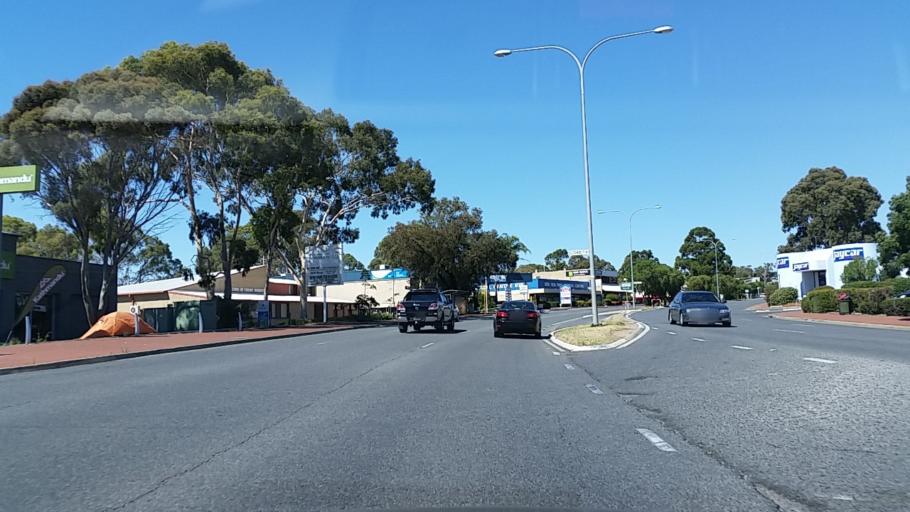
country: AU
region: South Australia
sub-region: Tea Tree Gully
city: Modbury
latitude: -34.8322
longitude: 138.6847
